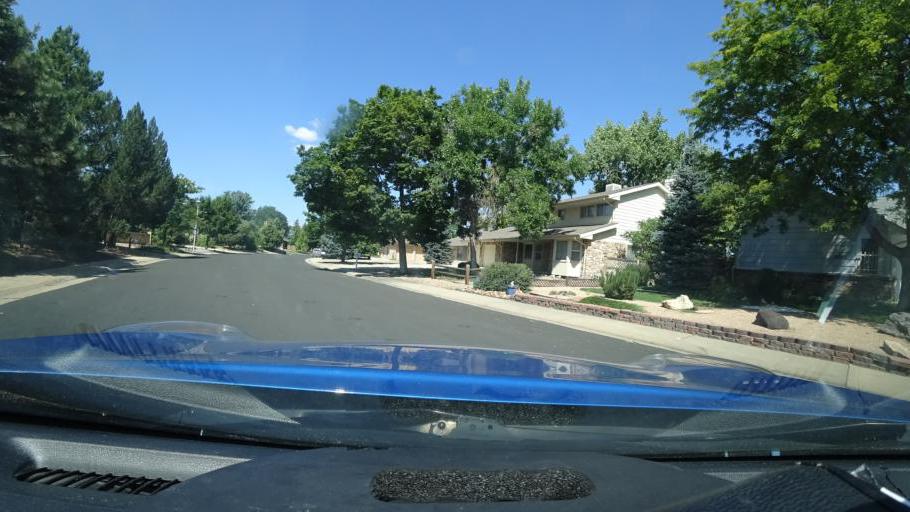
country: US
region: Colorado
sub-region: Adams County
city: Aurora
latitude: 39.7126
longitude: -104.8363
